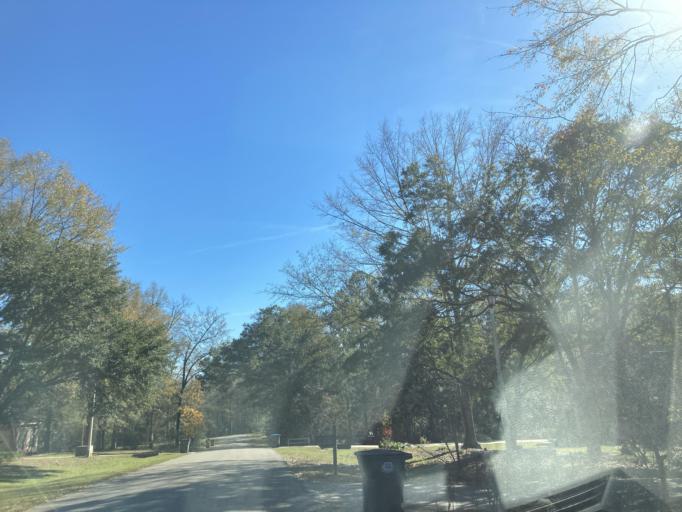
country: US
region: Mississippi
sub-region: Forrest County
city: Petal
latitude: 31.3318
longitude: -89.1686
